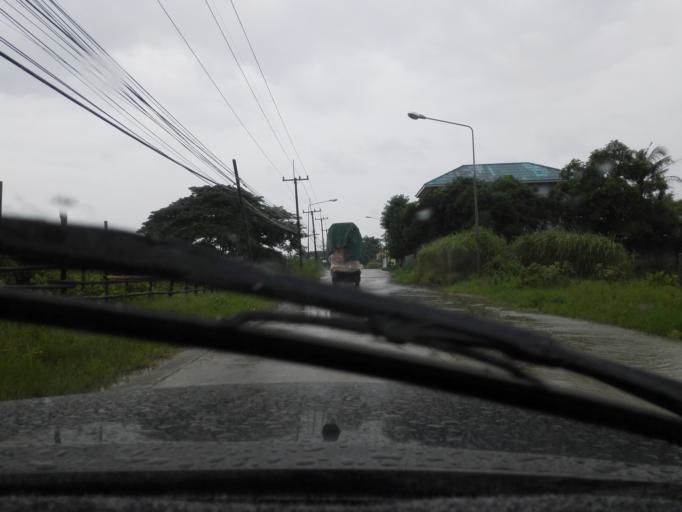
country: TH
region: Tak
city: Mae Sot
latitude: 16.6992
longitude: 98.5733
